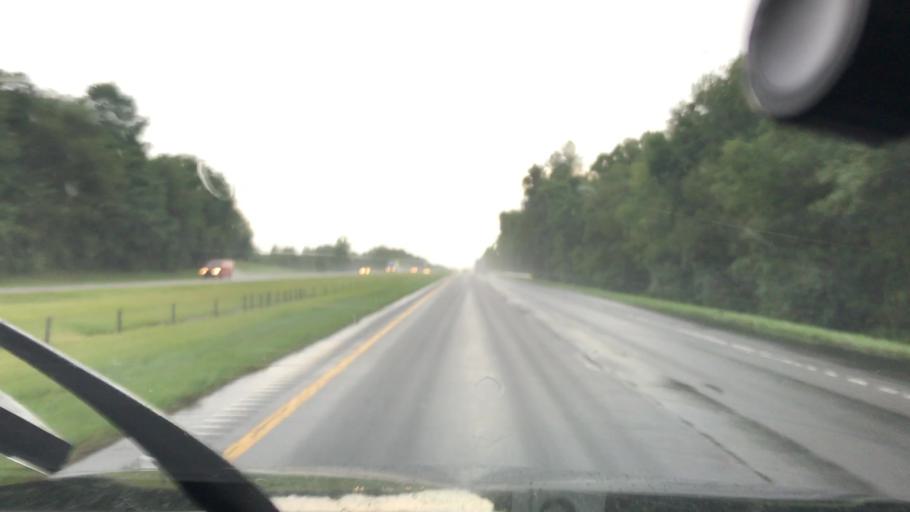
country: US
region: North Carolina
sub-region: Iredell County
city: Statesville
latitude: 35.9524
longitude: -80.8493
